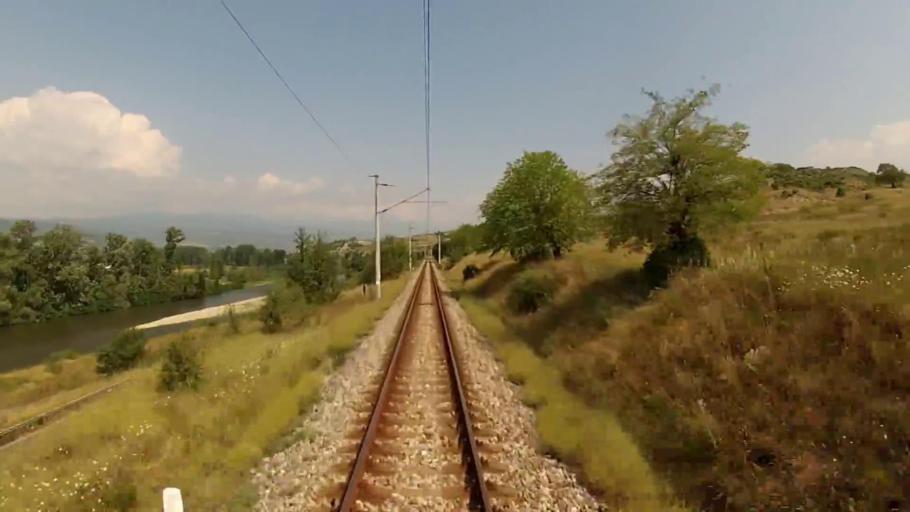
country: BG
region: Blagoevgrad
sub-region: Obshtina Strumyani
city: Strumyani
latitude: 41.6193
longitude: 23.2182
